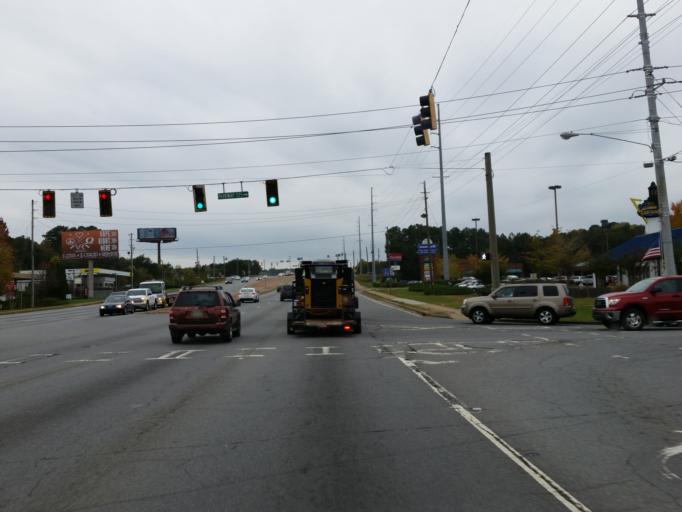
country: US
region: Georgia
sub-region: Cherokee County
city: Woodstock
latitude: 34.0861
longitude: -84.5308
